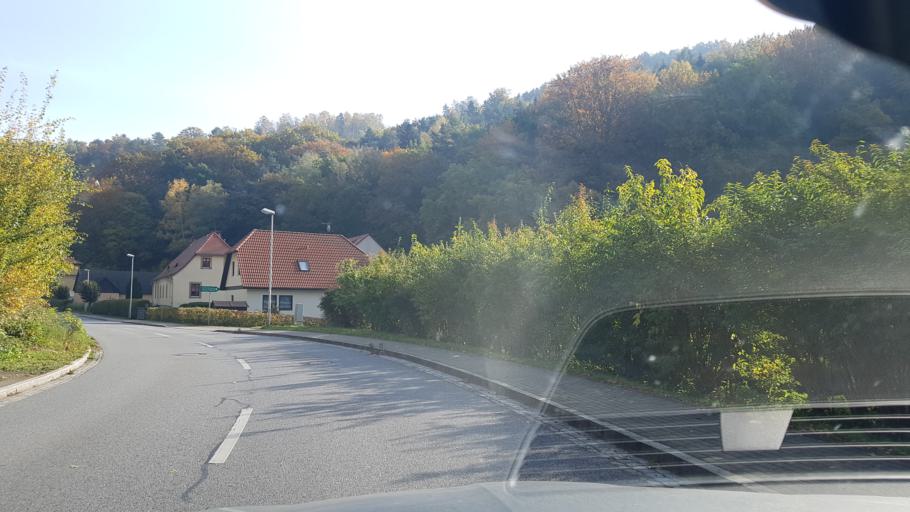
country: DE
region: Saxony
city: Konigstein
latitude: 50.9127
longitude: 14.0665
